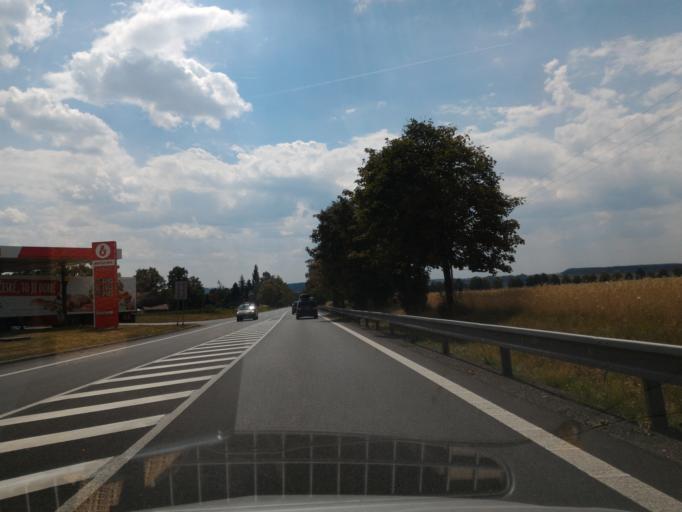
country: CZ
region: Vysocina
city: Habry
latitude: 49.7630
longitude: 15.4807
